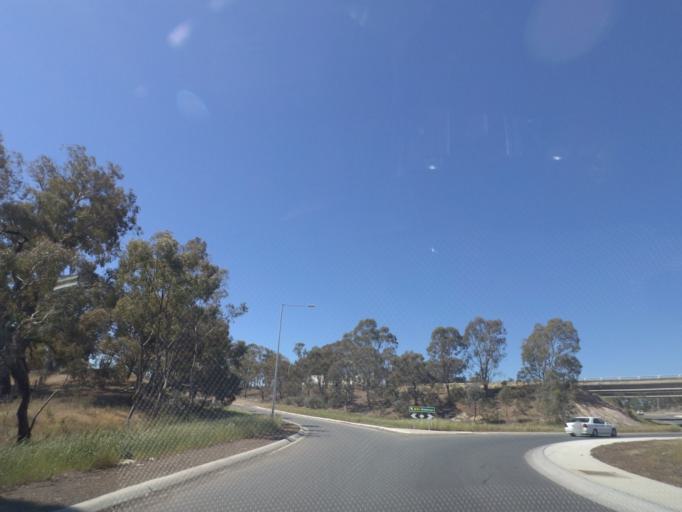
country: AU
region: Victoria
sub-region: Murrindindi
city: Kinglake West
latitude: -37.0308
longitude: 145.1002
